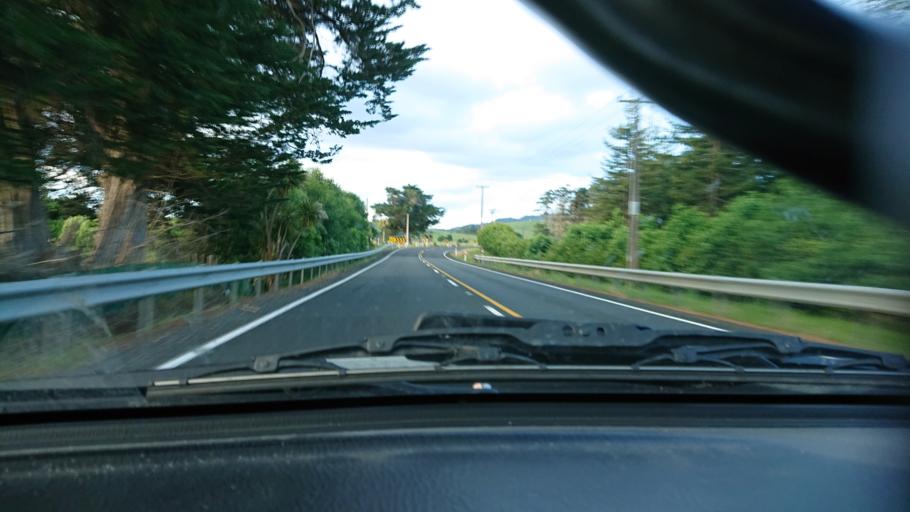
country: NZ
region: Auckland
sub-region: Auckland
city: Parakai
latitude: -36.4905
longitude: 174.4479
